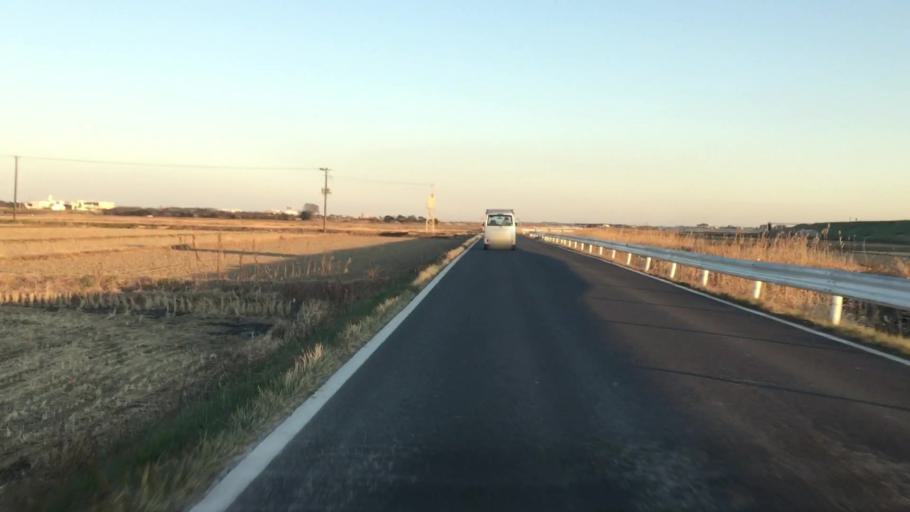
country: JP
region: Ibaraki
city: Moriya
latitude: 35.9009
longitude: 140.0096
